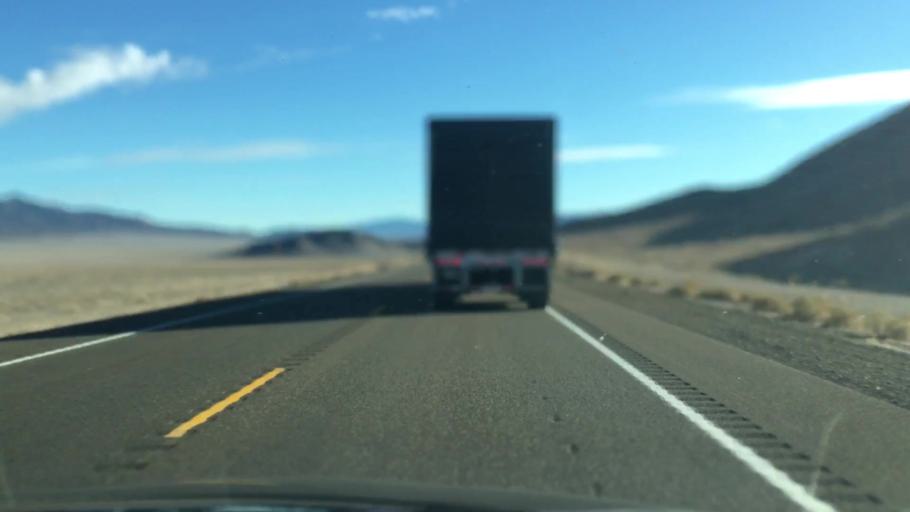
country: US
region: Nevada
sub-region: Nye County
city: Tonopah
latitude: 38.1671
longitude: -117.9548
